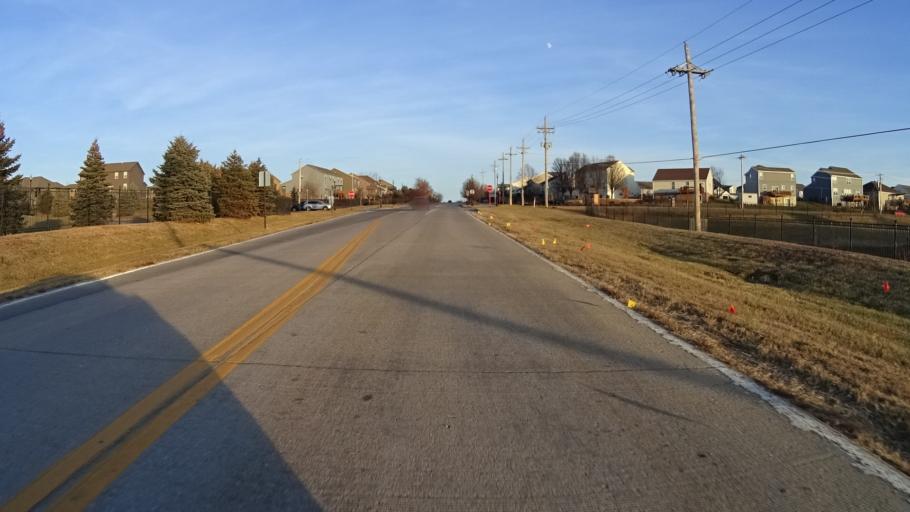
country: US
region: Nebraska
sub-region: Sarpy County
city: Papillion
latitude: 41.1326
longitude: -96.0632
